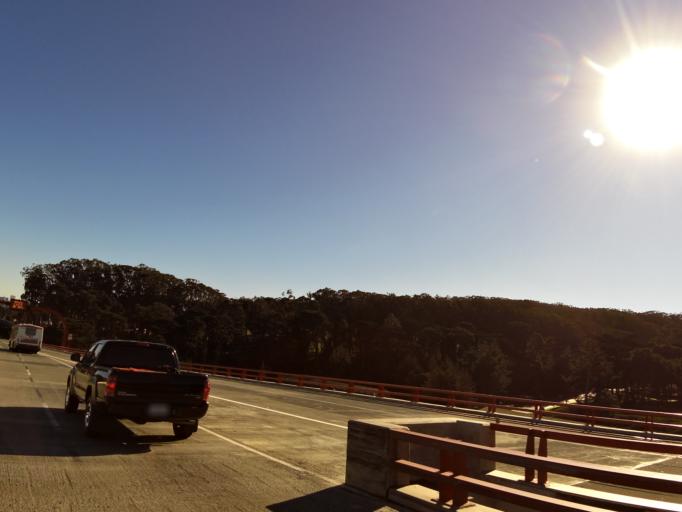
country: US
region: California
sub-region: San Francisco County
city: San Francisco
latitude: 37.8026
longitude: -122.4680
